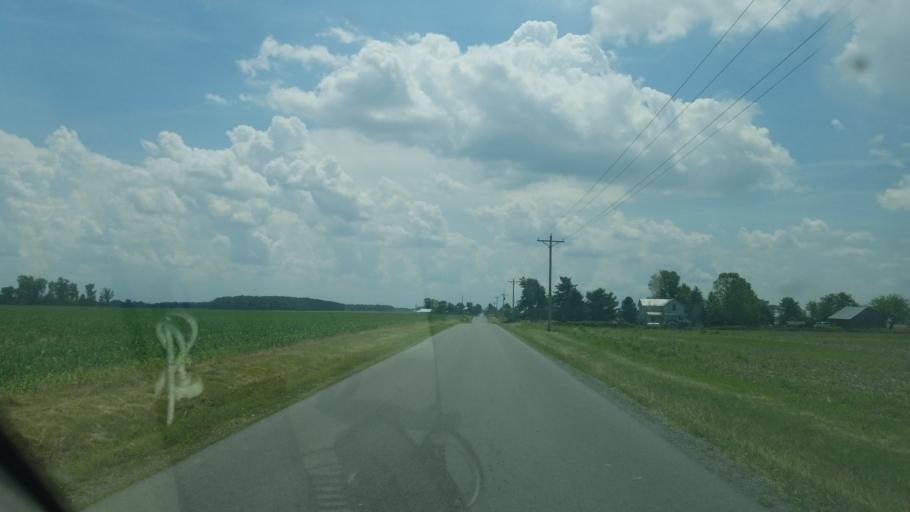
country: US
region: Ohio
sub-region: Hancock County
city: Arlington
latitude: 40.8546
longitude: -83.5998
